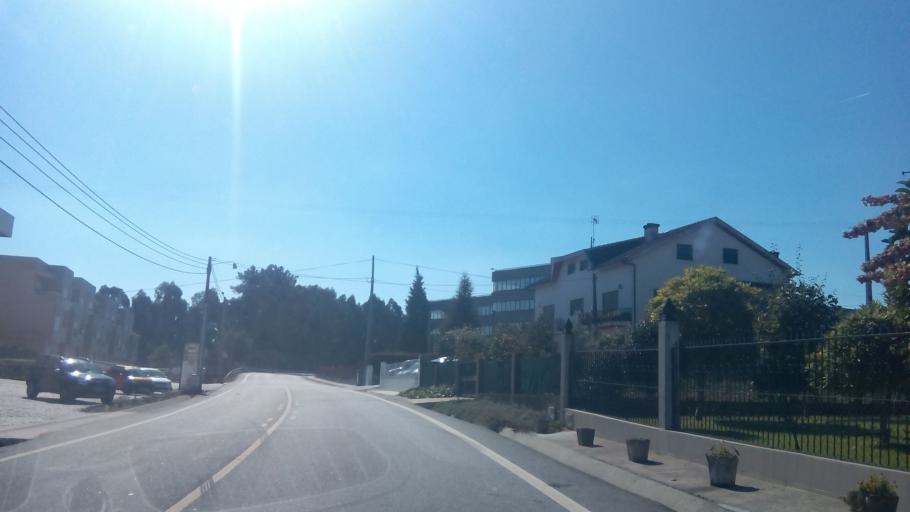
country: PT
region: Porto
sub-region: Lousada
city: Meinedo
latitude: 41.2548
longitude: -8.2136
